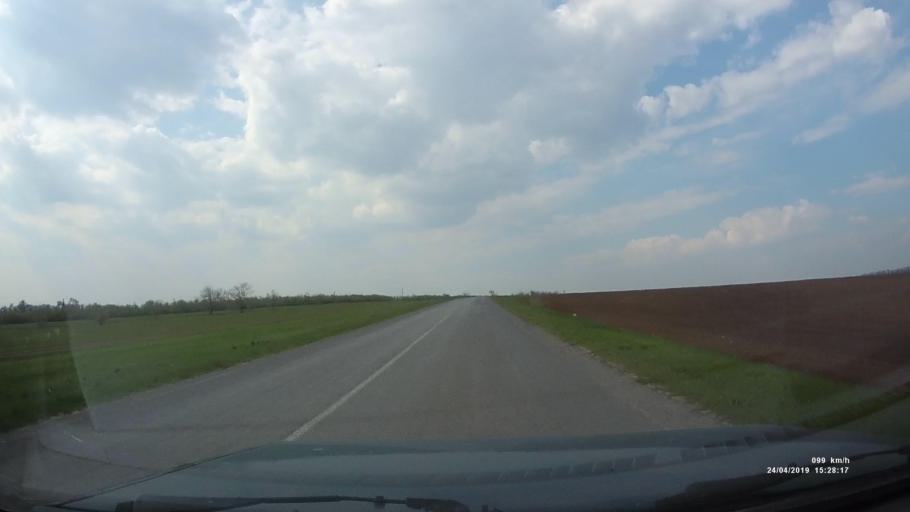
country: RU
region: Rostov
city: Remontnoye
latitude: 46.5768
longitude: 43.0194
